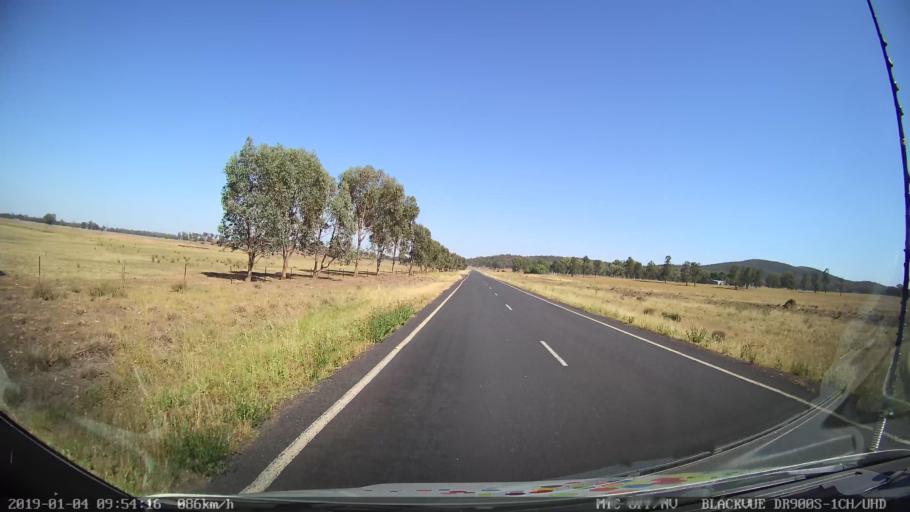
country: AU
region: New South Wales
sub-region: Cabonne
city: Canowindra
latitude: -33.5428
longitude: 148.4167
